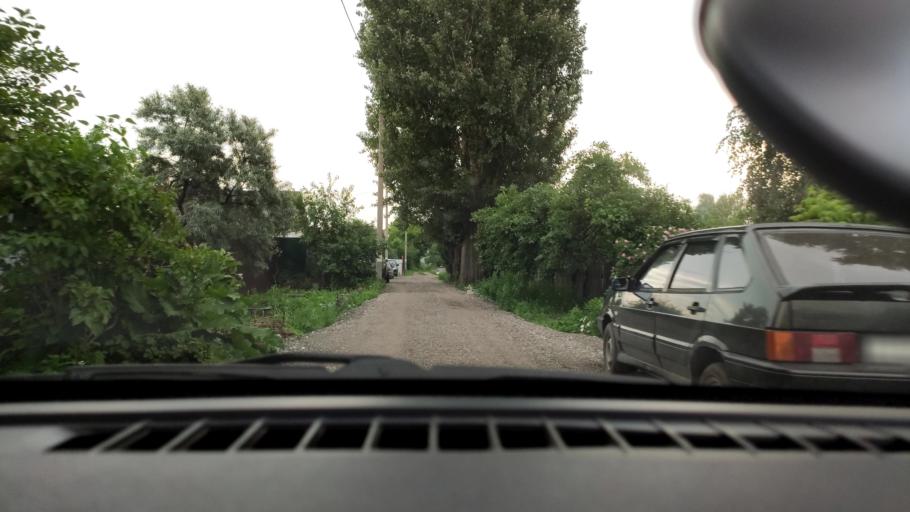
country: RU
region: Samara
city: Petra-Dubrava
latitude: 53.2649
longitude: 50.2912
